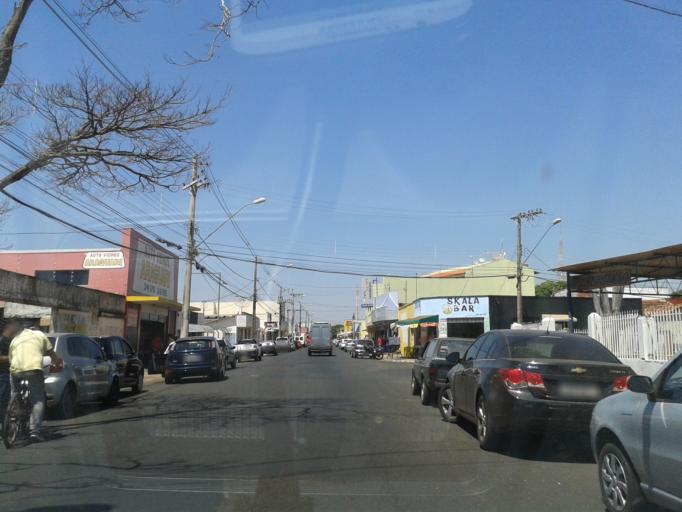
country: BR
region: Minas Gerais
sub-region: Araguari
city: Araguari
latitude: -18.6629
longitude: -48.1842
